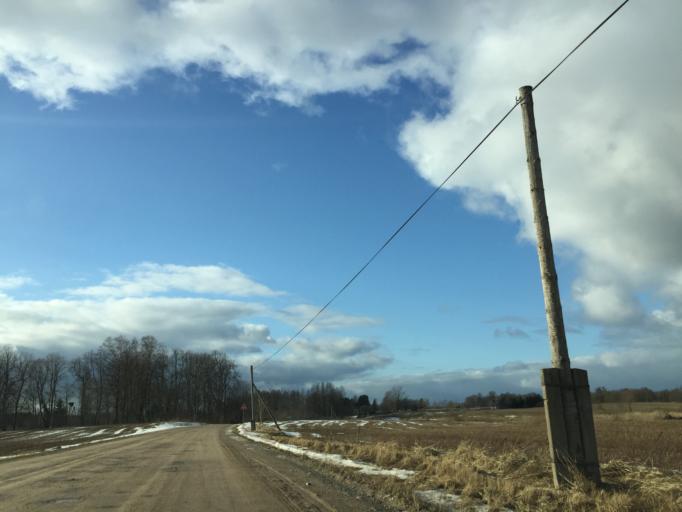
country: LV
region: Limbazu Rajons
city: Limbazi
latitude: 57.6117
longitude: 24.5941
